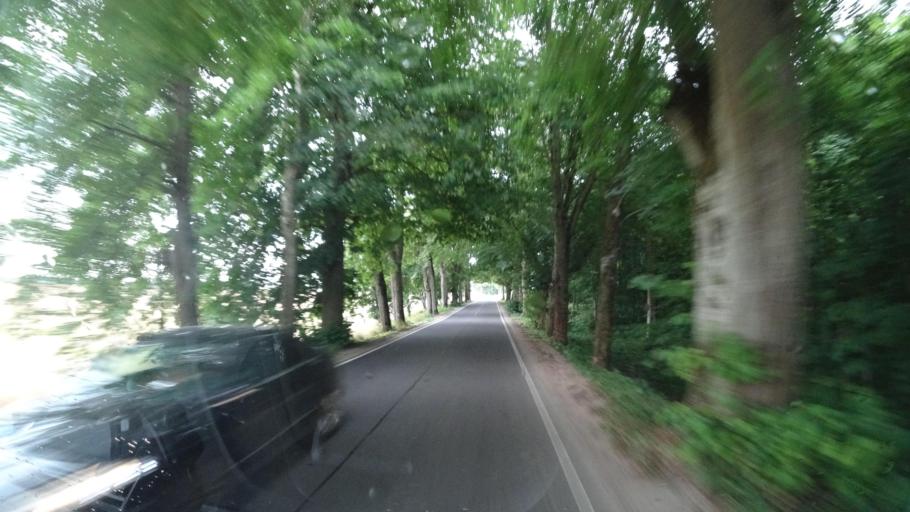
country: PL
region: Warmian-Masurian Voivodeship
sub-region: Powiat gizycki
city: Ryn
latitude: 53.9101
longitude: 21.5607
